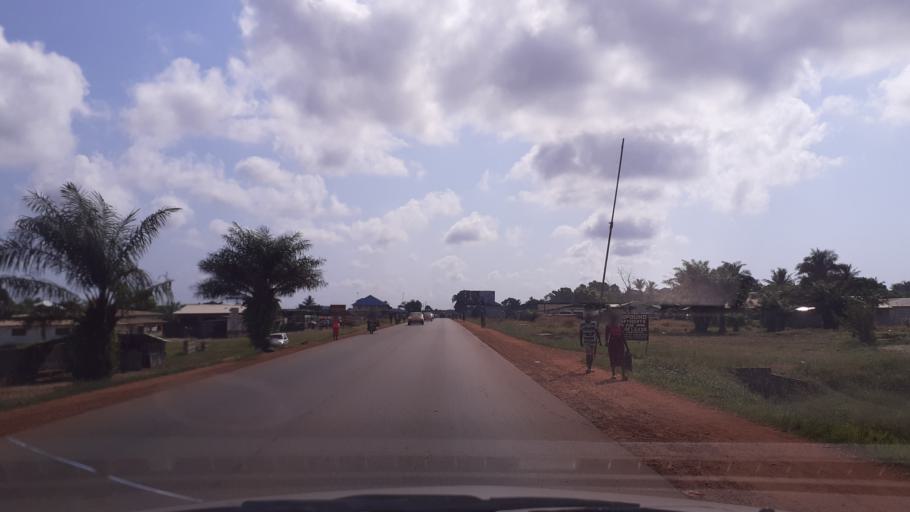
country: LR
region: Montserrado
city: Monrovia
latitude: 6.2244
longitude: -10.6105
